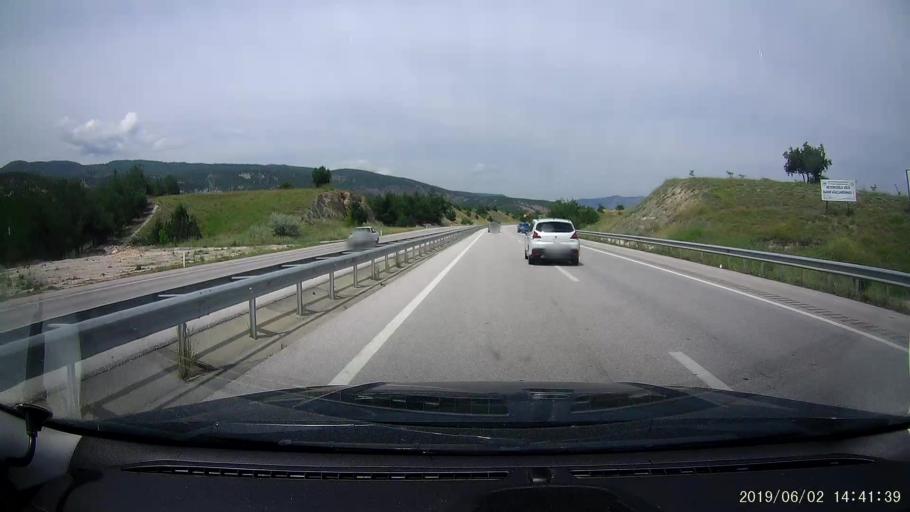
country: TR
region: Corum
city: Hacihamza
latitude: 41.0902
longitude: 34.3433
